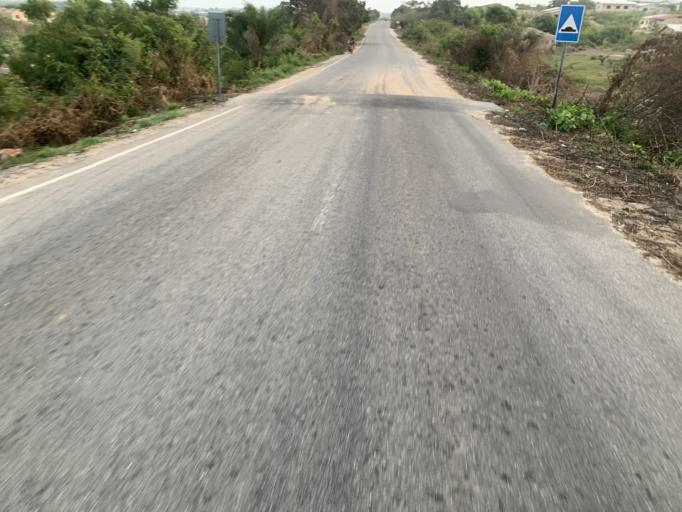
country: GH
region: Central
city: Winneba
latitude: 5.3734
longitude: -0.6069
